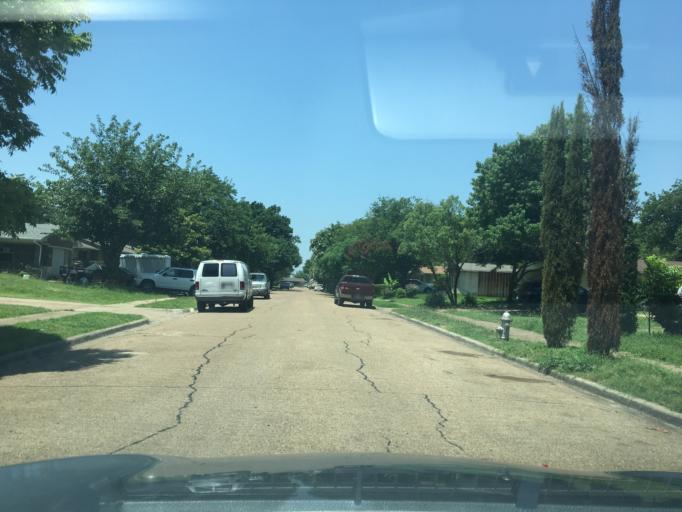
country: US
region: Texas
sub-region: Dallas County
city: Richardson
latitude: 32.9120
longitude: -96.6971
